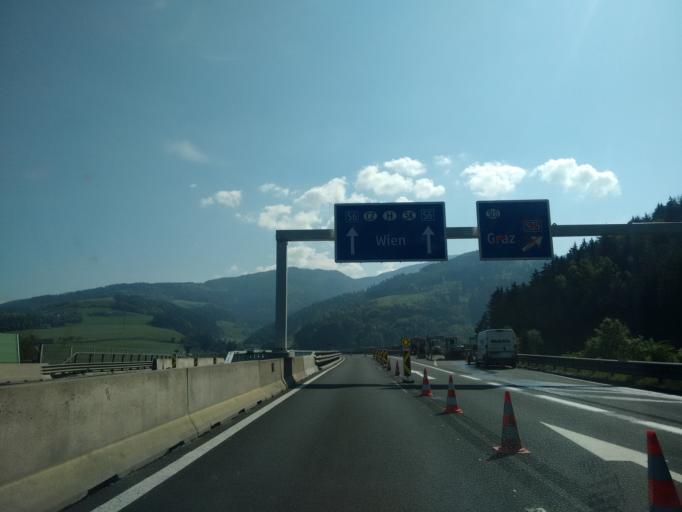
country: AT
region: Styria
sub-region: Politischer Bezirk Bruck-Muerzzuschlag
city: Bruck an der Mur
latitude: 47.4053
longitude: 15.2767
